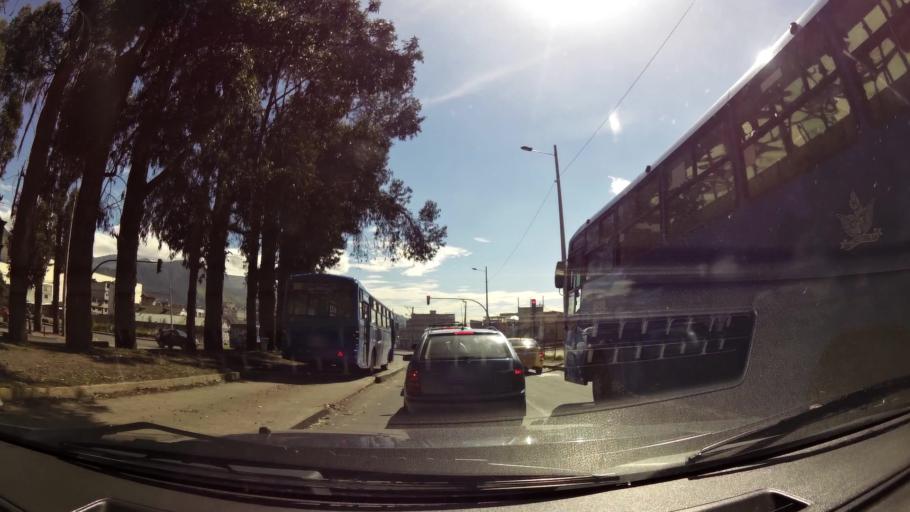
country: EC
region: Pichincha
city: Quito
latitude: -0.2835
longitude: -78.5546
